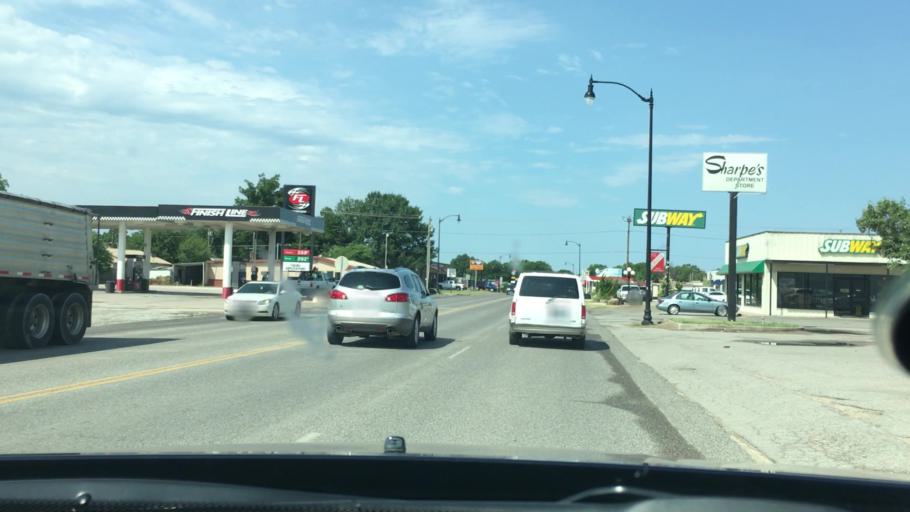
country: US
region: Oklahoma
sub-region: Murray County
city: Davis
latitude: 34.5036
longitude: -97.1227
